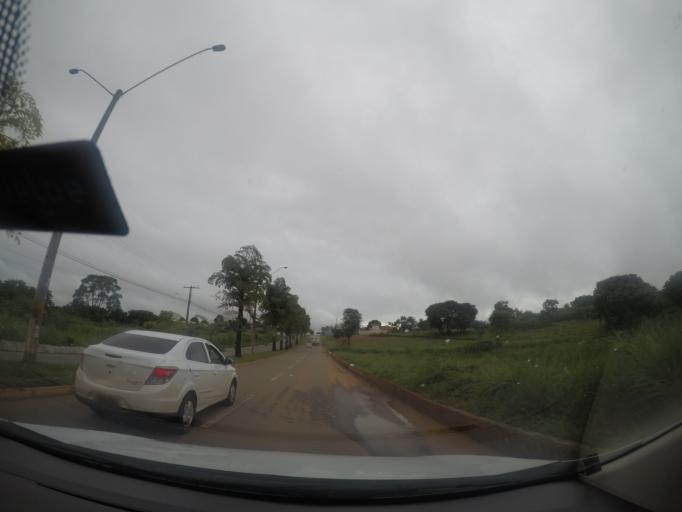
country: BR
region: Goias
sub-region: Aparecida De Goiania
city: Aparecida de Goiania
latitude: -16.7601
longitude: -49.3225
